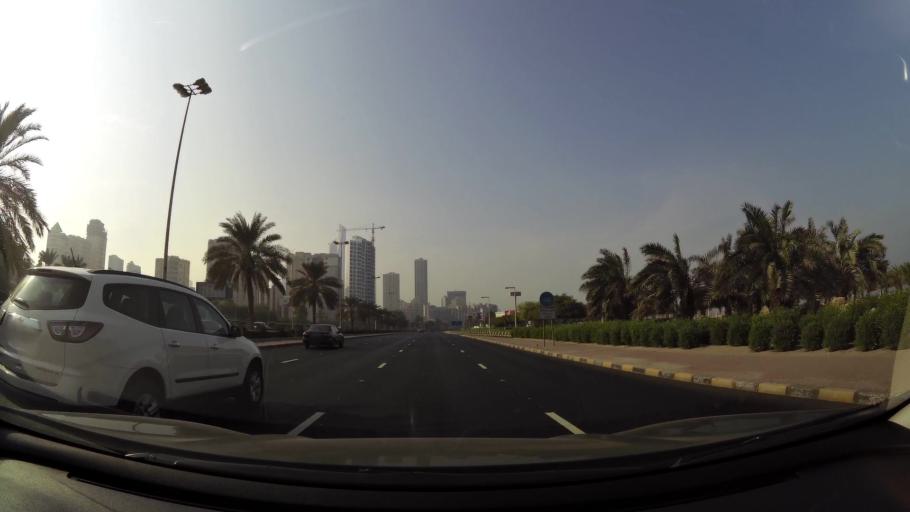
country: KW
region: Al Asimah
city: Ad Dasmah
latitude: 29.3717
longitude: 48.0089
